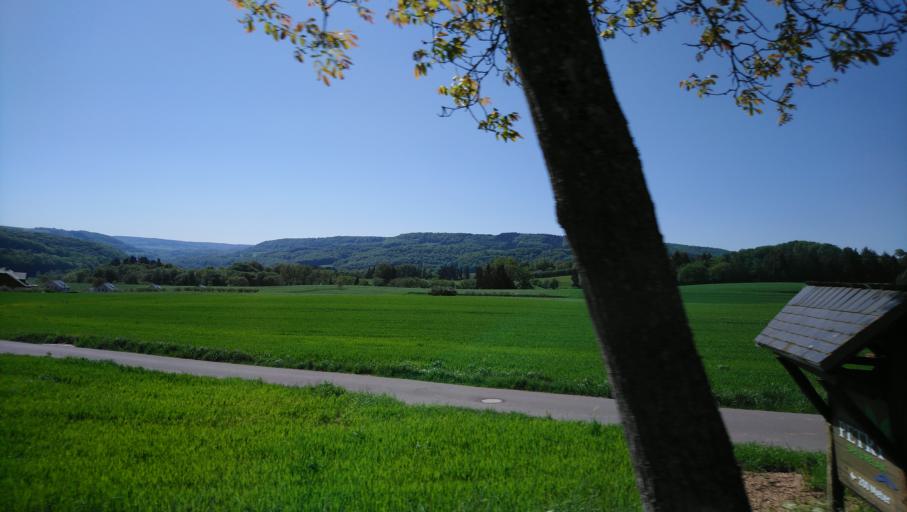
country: DE
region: Rheinland-Pfalz
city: Gentingen
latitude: 49.9151
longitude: 6.2190
